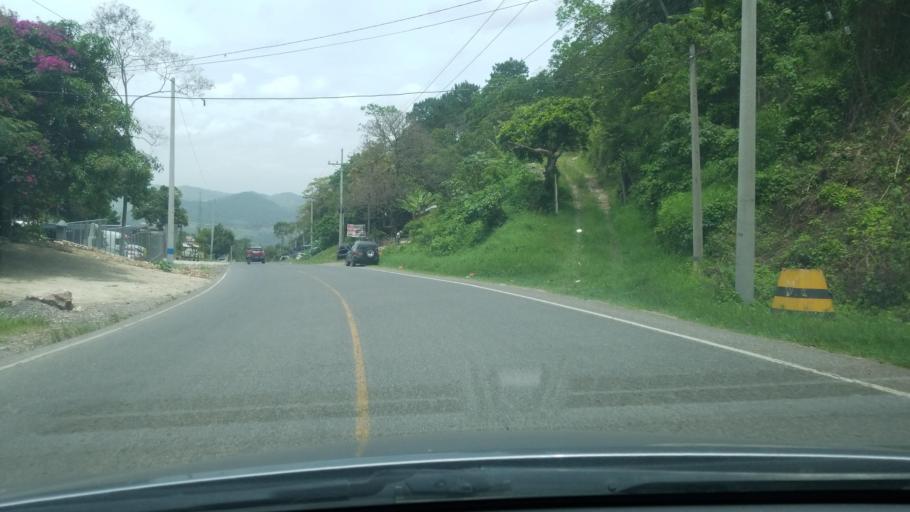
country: HN
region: Copan
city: Santa Rosa de Copan
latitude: 14.7474
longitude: -88.7745
